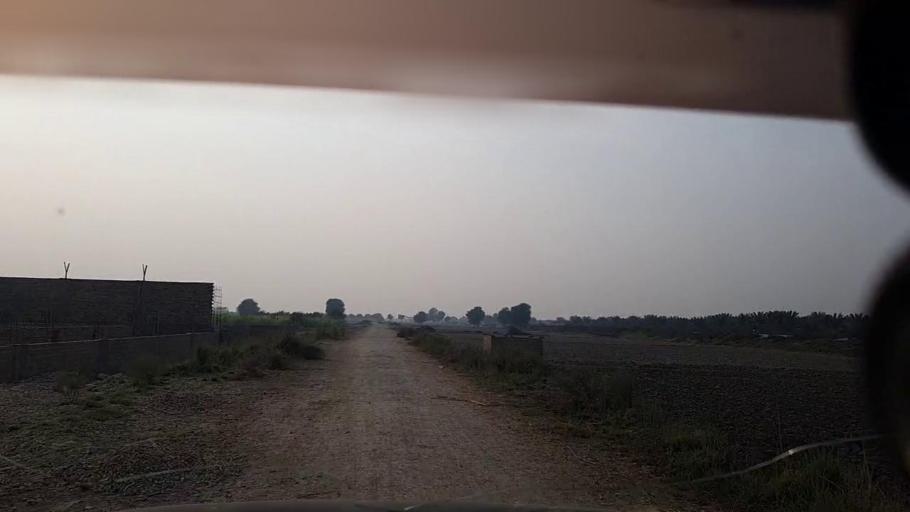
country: PK
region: Sindh
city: Gambat
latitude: 27.4355
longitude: 68.6052
